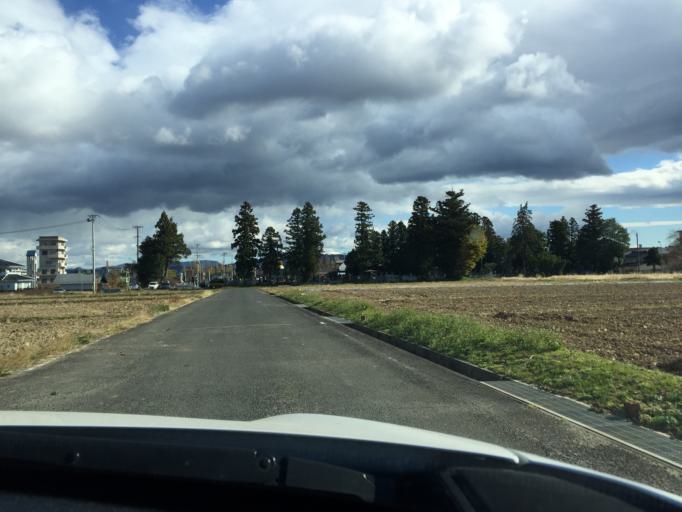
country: JP
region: Fukushima
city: Fukushima-shi
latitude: 37.7360
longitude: 140.4146
